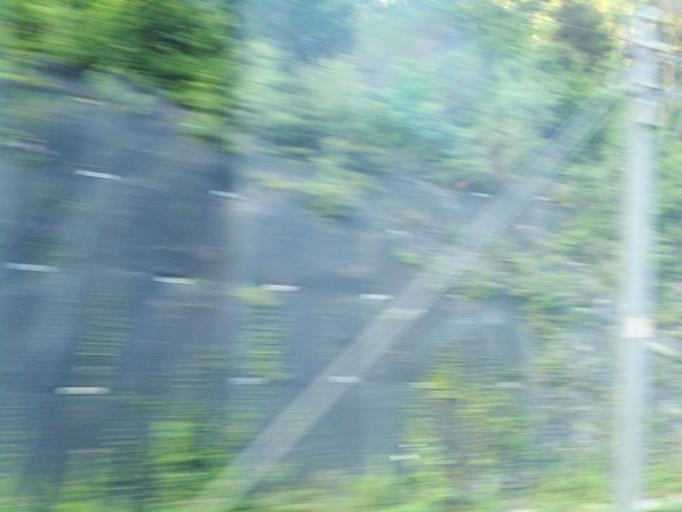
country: RO
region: Prahova
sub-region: Comuna Comarnic
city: Posada
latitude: 45.2890
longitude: 25.6103
